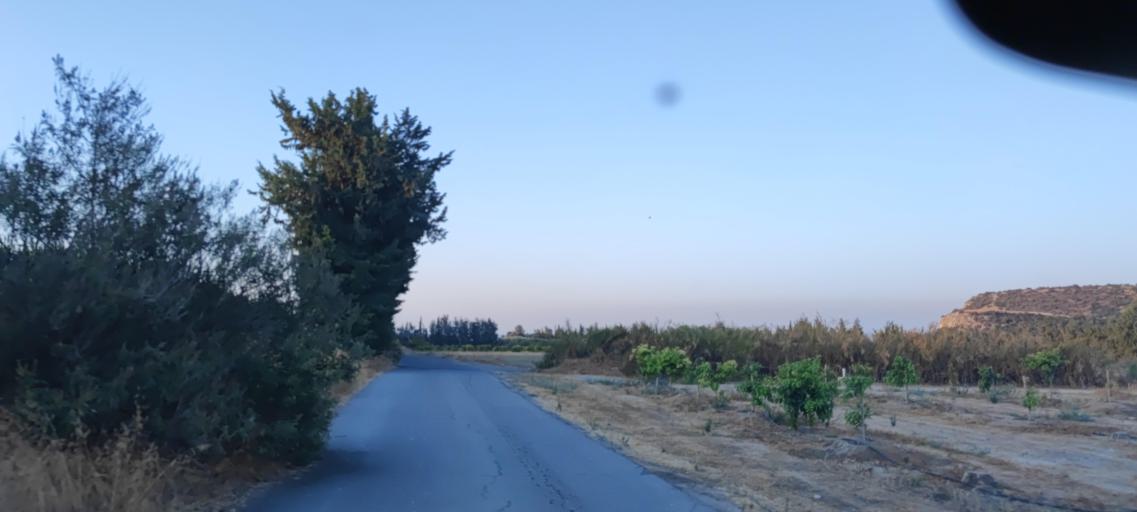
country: CY
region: Limassol
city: Sotira
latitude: 34.6731
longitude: 32.7961
